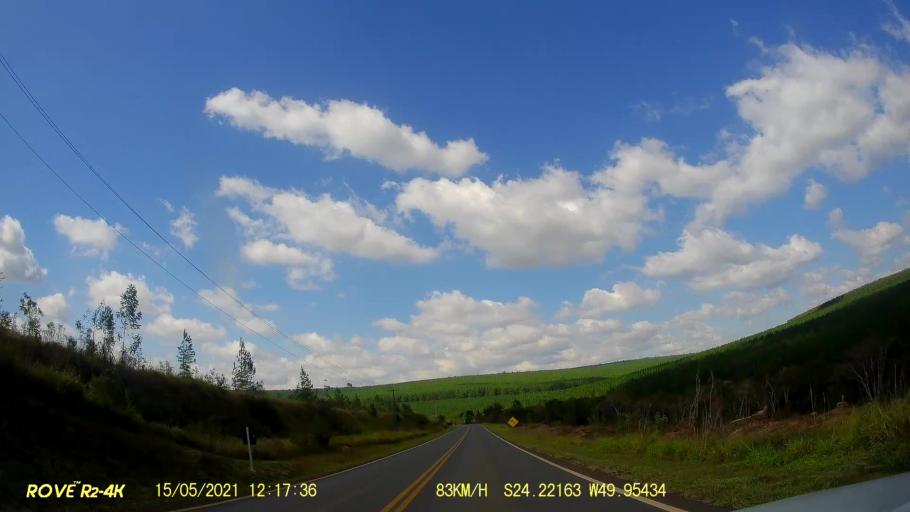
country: BR
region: Parana
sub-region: Jaguariaiva
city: Jaguariaiva
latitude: -24.2217
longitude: -49.9547
